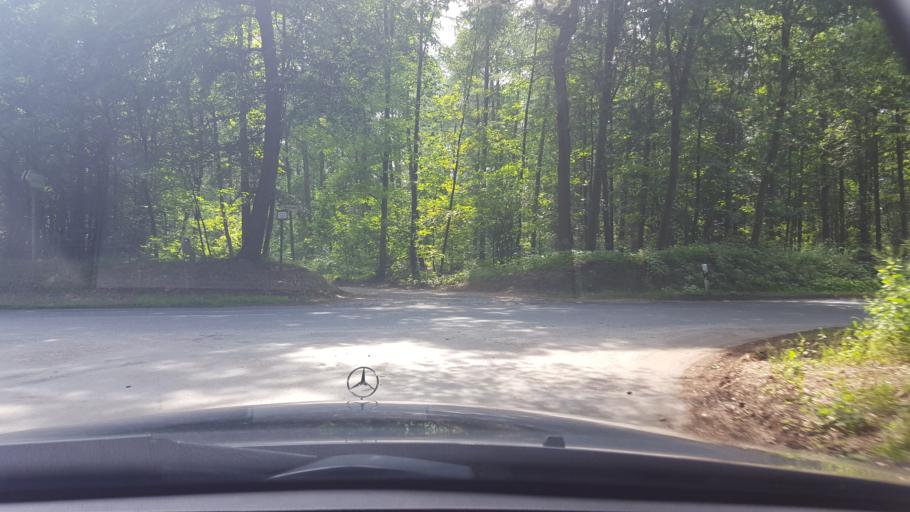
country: DE
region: North Rhine-Westphalia
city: Oer-Erkenschwick
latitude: 51.7289
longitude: 7.2835
